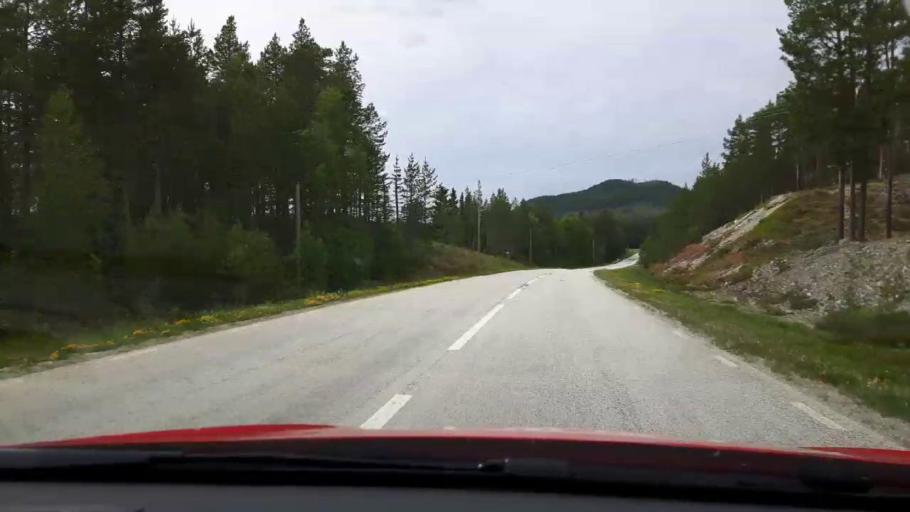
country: SE
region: Jaemtland
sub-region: Harjedalens Kommun
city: Sveg
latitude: 62.4115
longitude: 13.6446
